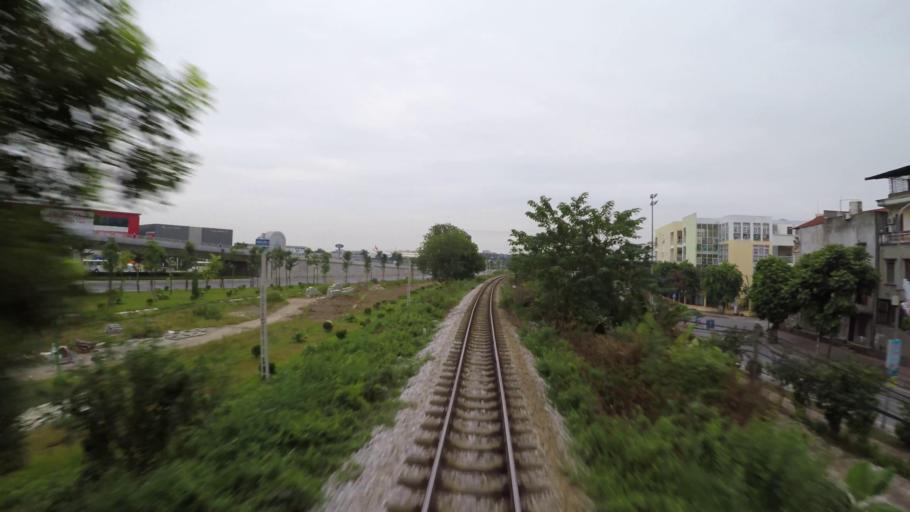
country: VN
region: Ha Noi
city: Trau Quy
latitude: 21.0178
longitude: 105.9427
